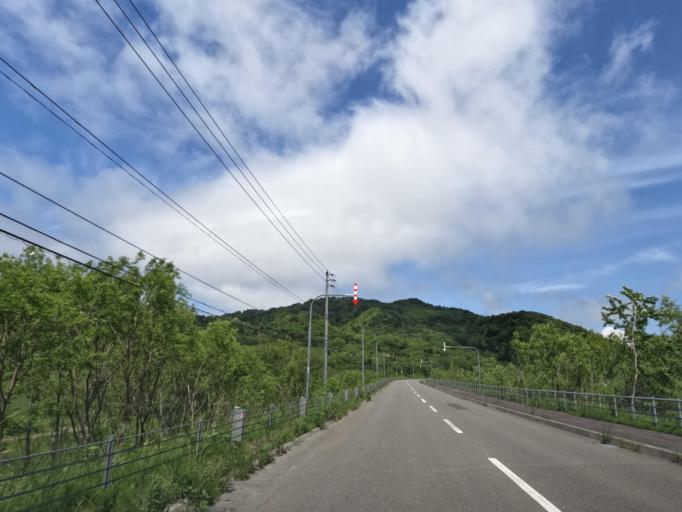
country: JP
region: Hokkaido
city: Tobetsu
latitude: 43.3159
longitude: 141.5572
